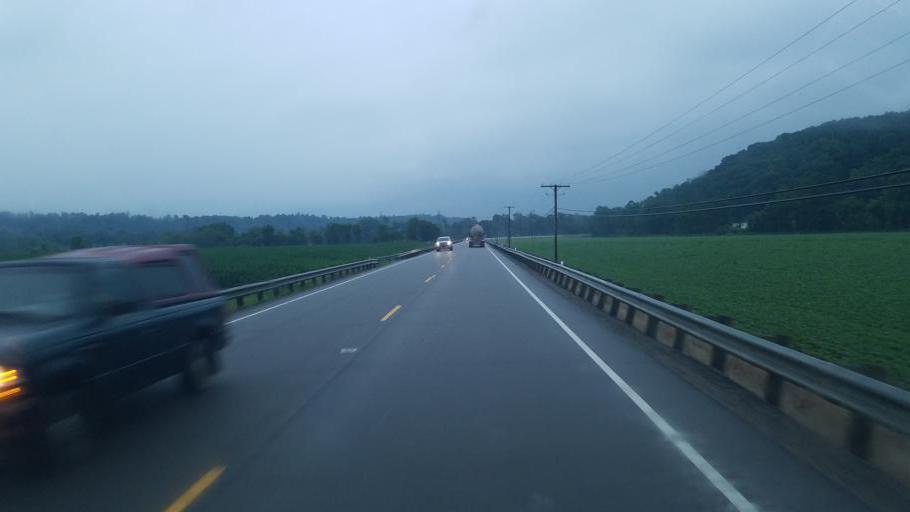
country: US
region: Ohio
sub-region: Coshocton County
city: Coshocton
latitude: 40.3027
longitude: -81.9047
